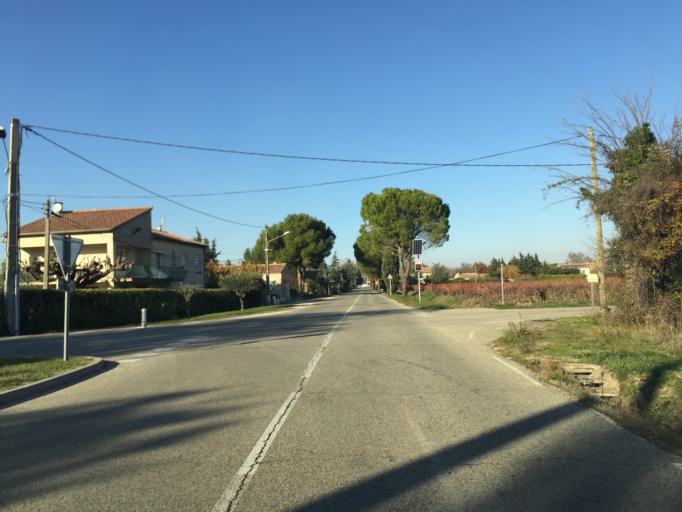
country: FR
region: Provence-Alpes-Cote d'Azur
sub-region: Departement du Vaucluse
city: Camaret-sur-Aigues
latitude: 44.1590
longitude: 4.8764
